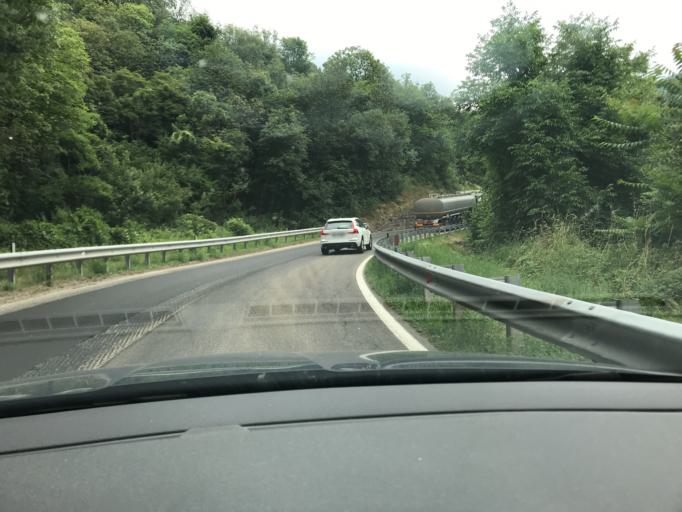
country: IT
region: Trentino-Alto Adige
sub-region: Bolzano
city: Laion
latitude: 46.6012
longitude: 11.5670
